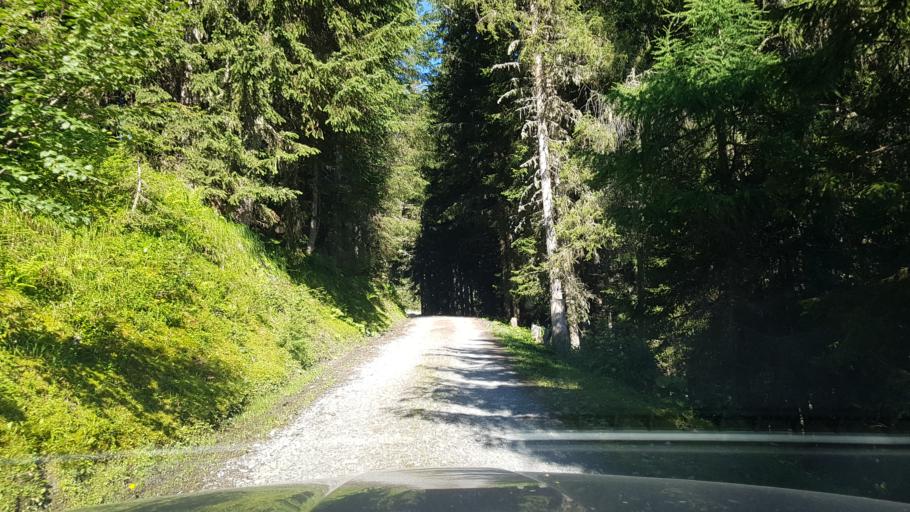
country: AT
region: Salzburg
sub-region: Politischer Bezirk Sankt Johann im Pongau
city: Dorfgastein
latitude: 47.2443
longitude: 13.0690
